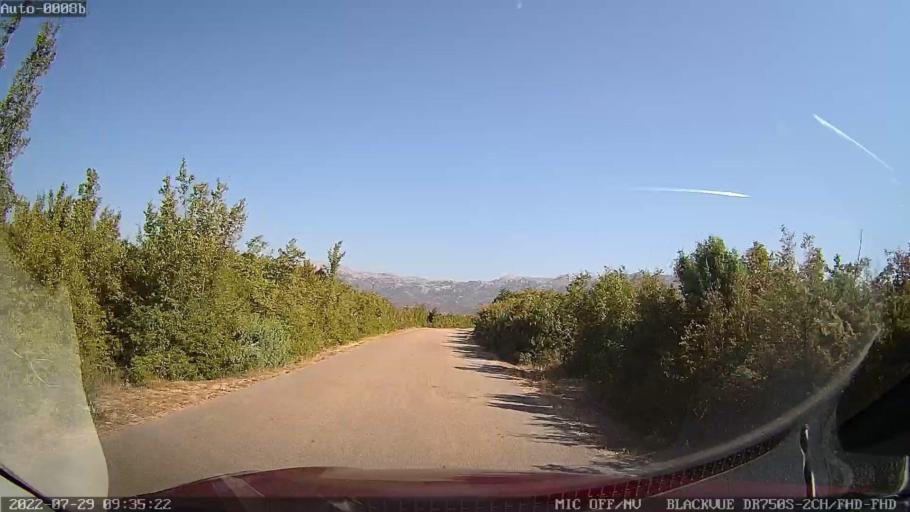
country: HR
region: Zadarska
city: Obrovac
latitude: 44.1854
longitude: 15.7324
